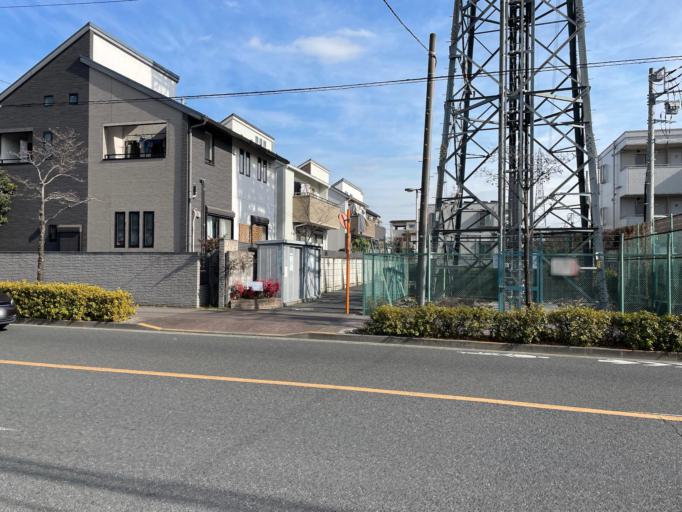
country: JP
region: Tokyo
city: Kamirenjaku
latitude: 35.6905
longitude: 139.5378
